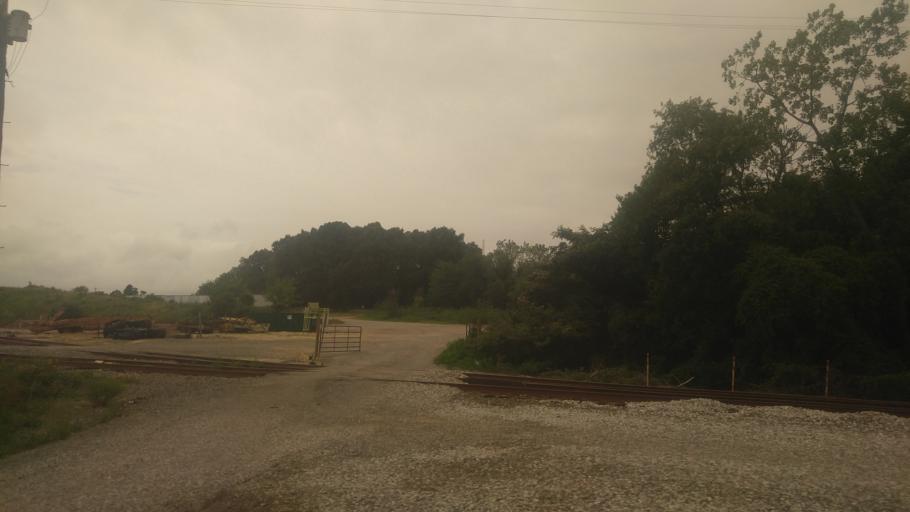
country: US
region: Virginia
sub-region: Henrico County
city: Dumbarton
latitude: 37.5881
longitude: -77.4806
